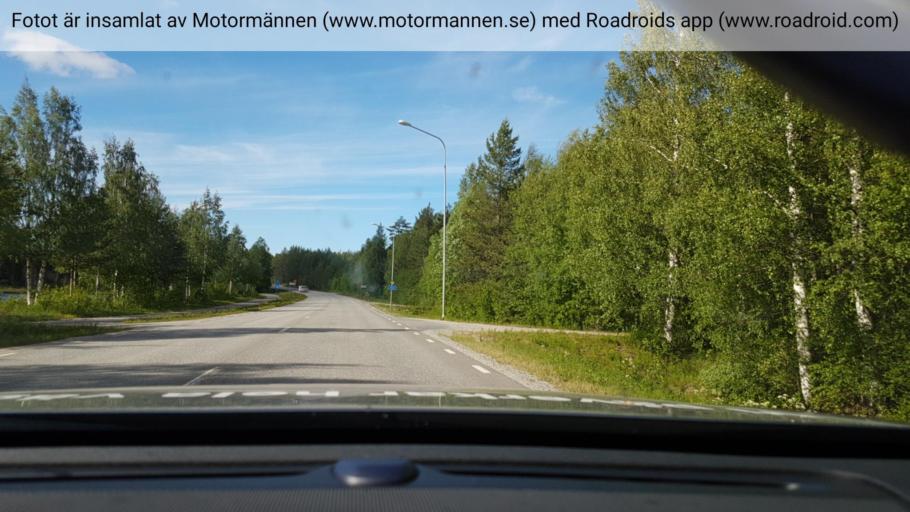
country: SE
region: Vaesterbotten
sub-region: Lycksele Kommun
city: Lycksele
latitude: 64.6088
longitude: 18.6979
